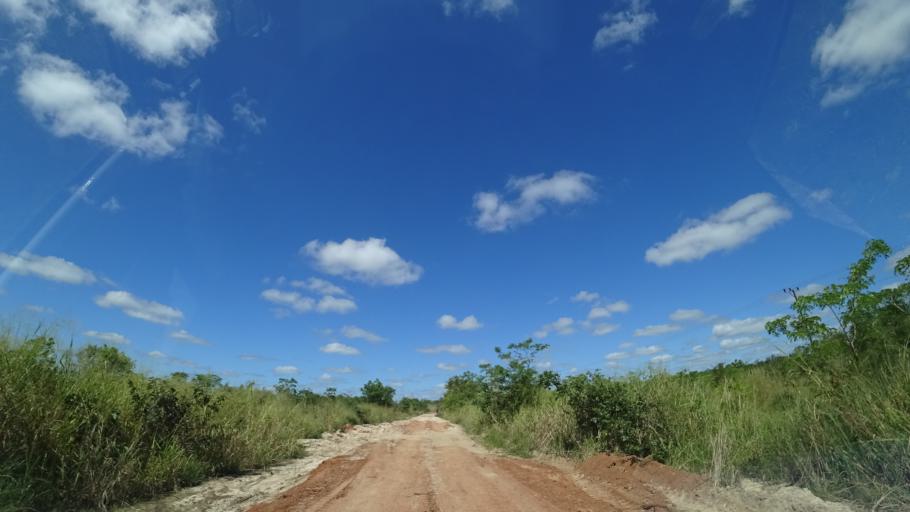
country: MZ
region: Sofala
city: Dondo
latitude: -19.2996
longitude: 34.6911
